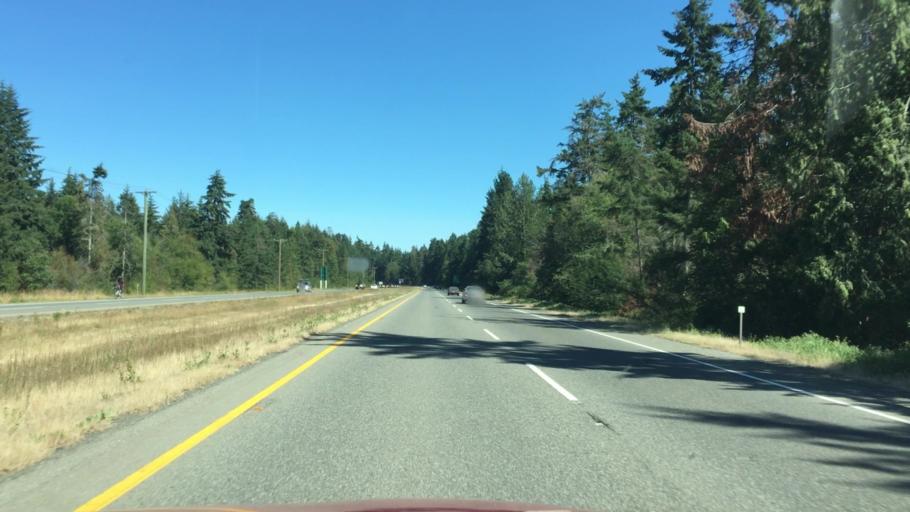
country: CA
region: British Columbia
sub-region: Regional District of Nanaimo
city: Parksville
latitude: 49.2998
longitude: -124.2898
